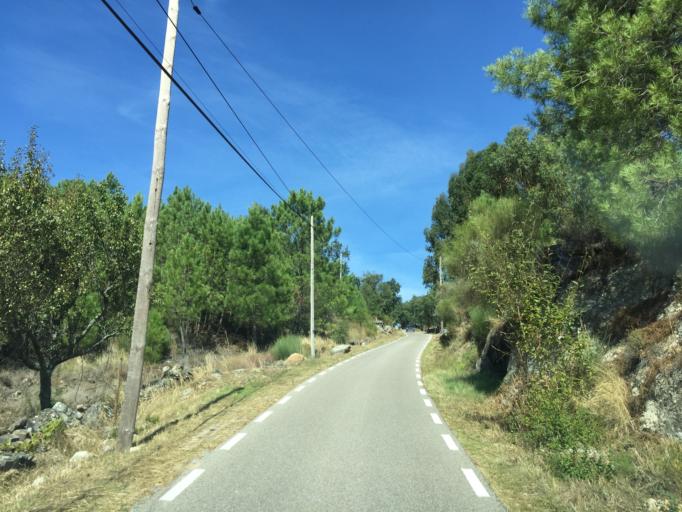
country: PT
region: Portalegre
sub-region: Marvao
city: Marvao
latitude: 39.3978
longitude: -7.3896
